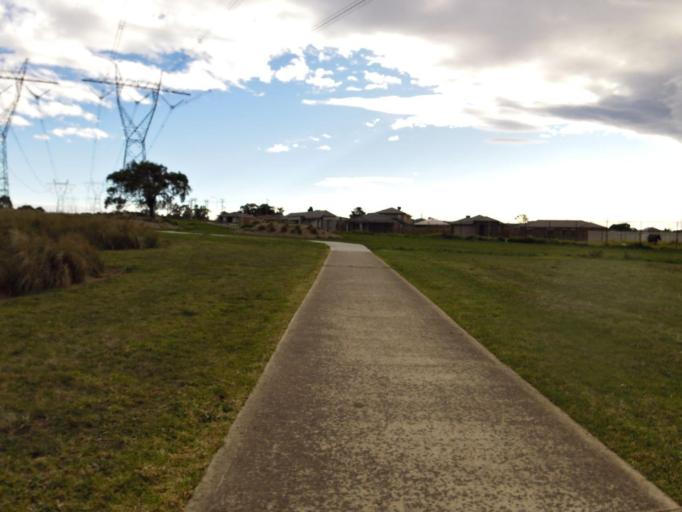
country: AU
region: Victoria
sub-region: Whittlesea
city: Epping
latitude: -37.6260
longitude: 145.0341
